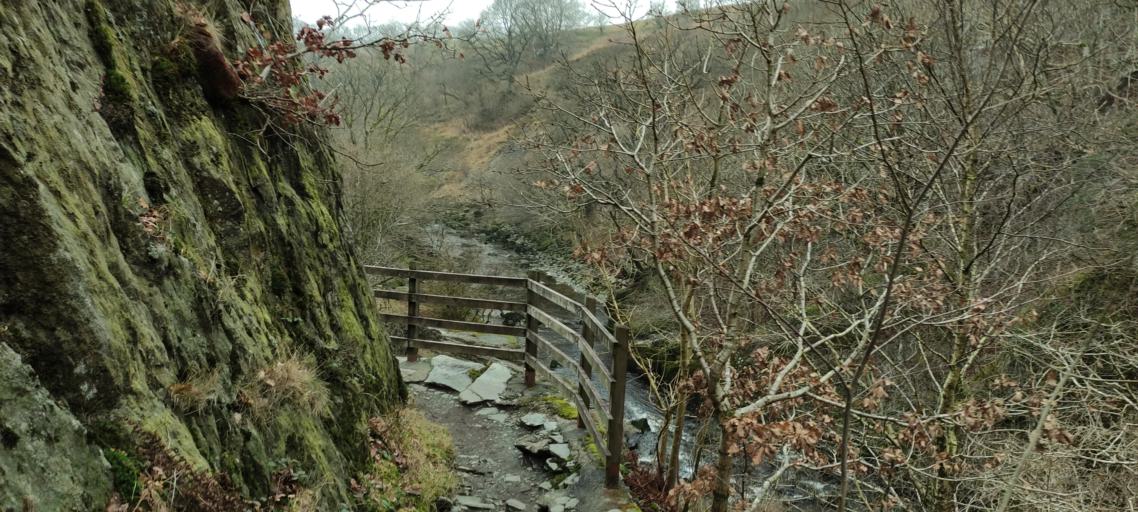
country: GB
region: England
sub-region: North Yorkshire
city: Ingleton
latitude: 54.1630
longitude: -2.4586
